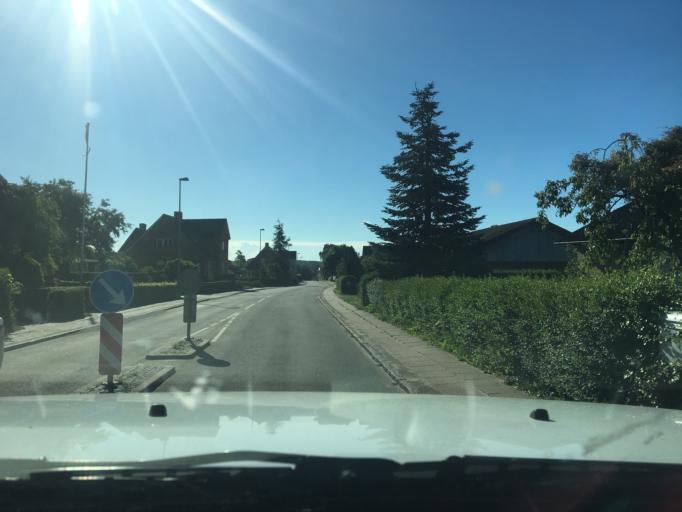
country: DK
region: Central Jutland
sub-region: Syddjurs Kommune
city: Hornslet
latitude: 56.3211
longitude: 10.3073
